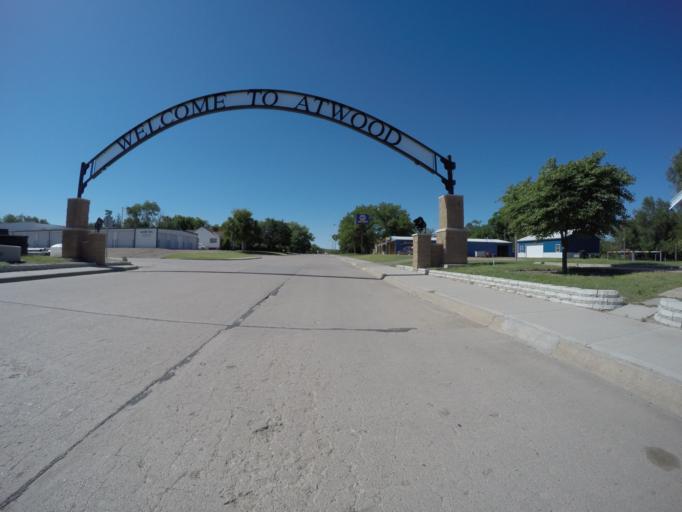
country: US
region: Kansas
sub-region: Rawlins County
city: Atwood
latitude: 39.8124
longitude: -101.0423
